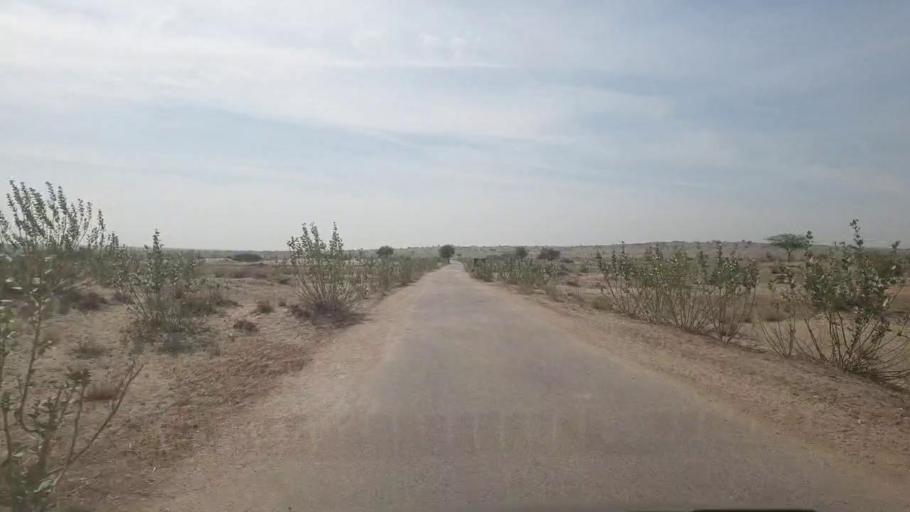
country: PK
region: Sindh
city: Umarkot
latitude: 25.2857
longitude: 69.7287
